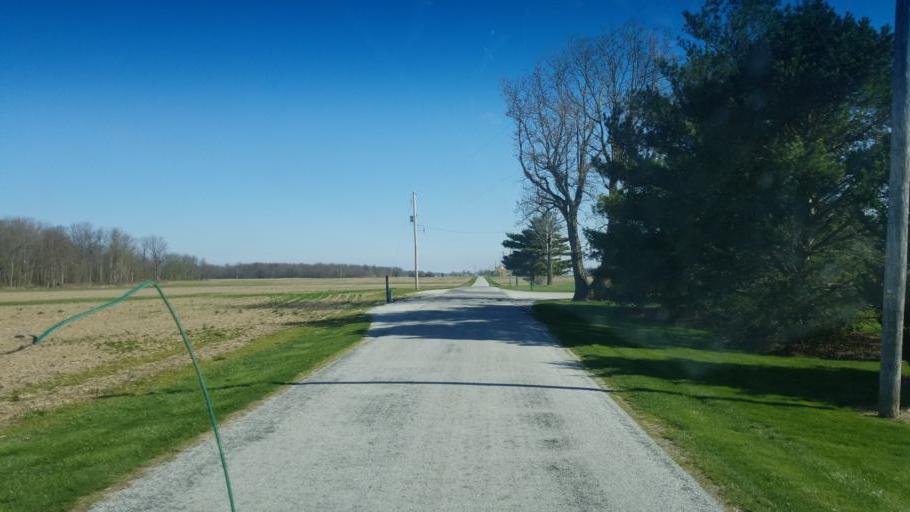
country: US
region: Ohio
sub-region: Hardin County
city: Kenton
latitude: 40.6680
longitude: -83.5620
